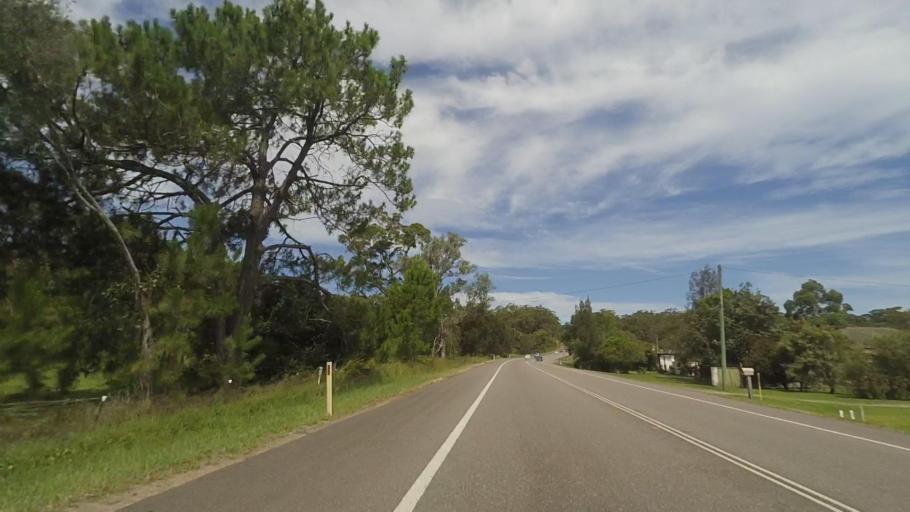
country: AU
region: New South Wales
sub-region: Port Stephens Shire
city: Medowie
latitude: -32.7888
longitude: 151.9367
